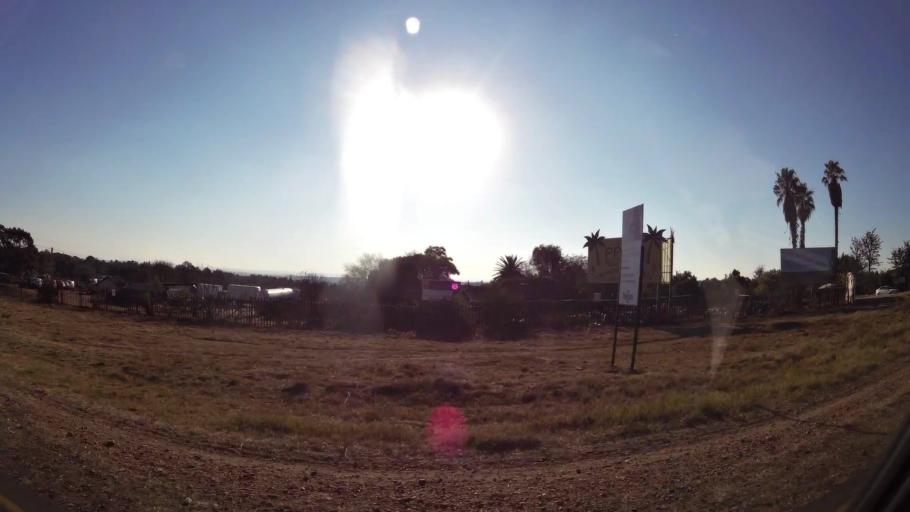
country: ZA
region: Gauteng
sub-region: City of Johannesburg Metropolitan Municipality
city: Diepsloot
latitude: -25.9909
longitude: 28.0507
